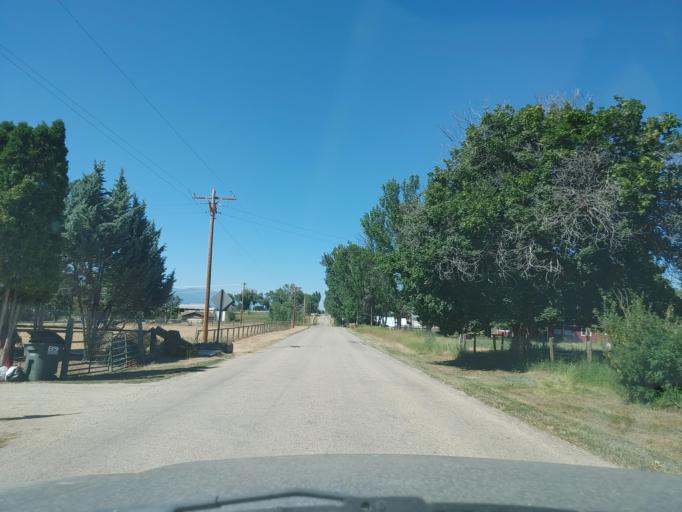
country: US
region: Montana
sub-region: Ravalli County
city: Hamilton
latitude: 46.3259
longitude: -114.0613
